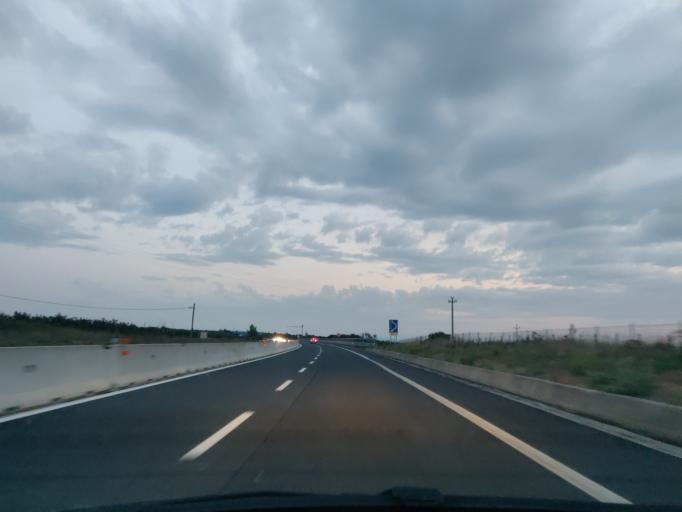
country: IT
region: Latium
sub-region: Provincia di Viterbo
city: Blera
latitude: 42.3508
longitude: 11.9812
